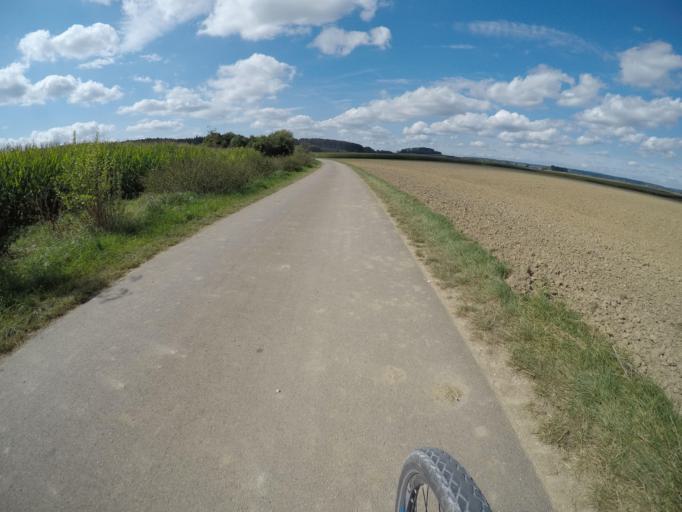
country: DE
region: Bavaria
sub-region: Swabia
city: Ziertheim
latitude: 48.6263
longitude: 10.3923
